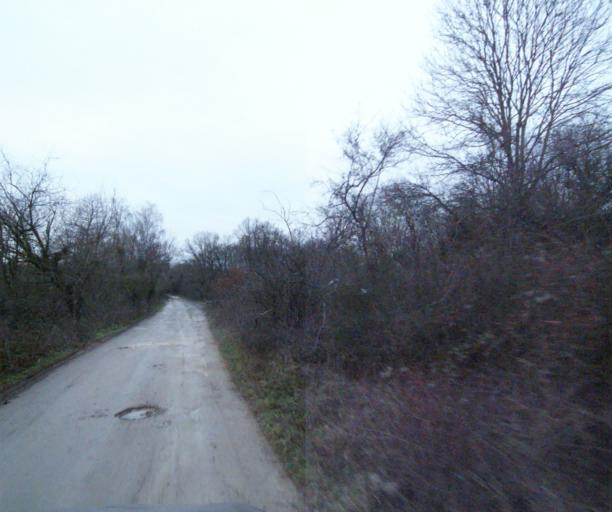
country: FR
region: Ile-de-France
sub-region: Departement de Seine-et-Marne
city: Longperrier
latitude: 49.0626
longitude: 2.6588
